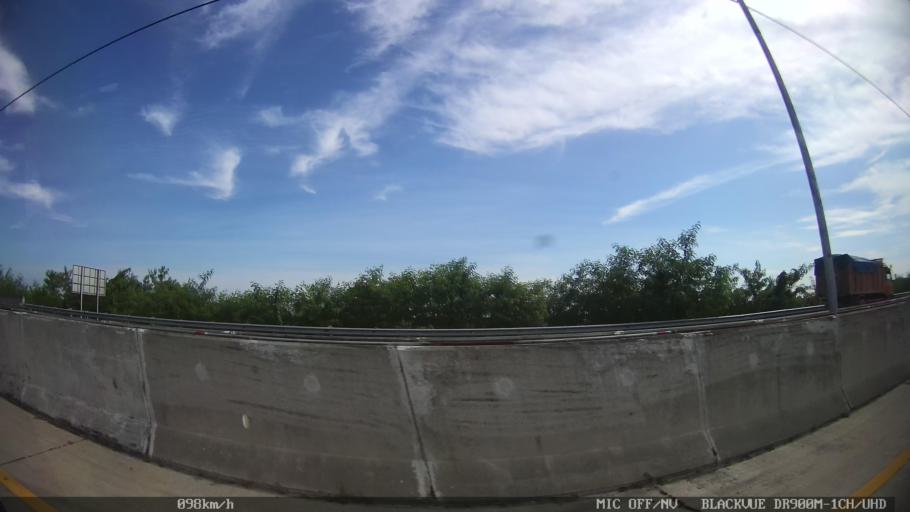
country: ID
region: North Sumatra
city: Sunggal
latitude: 3.6425
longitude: 98.5644
